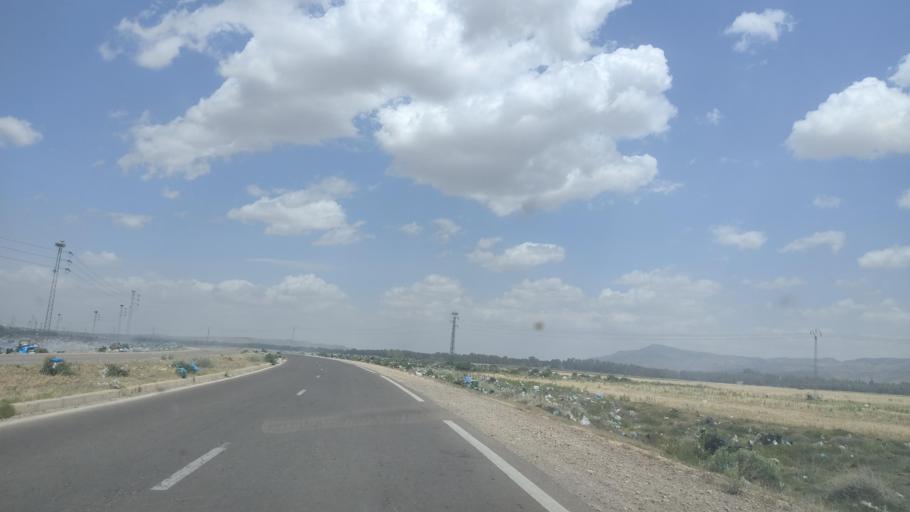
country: TN
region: Al Qasrayn
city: Kasserine
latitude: 35.1976
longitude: 8.8498
